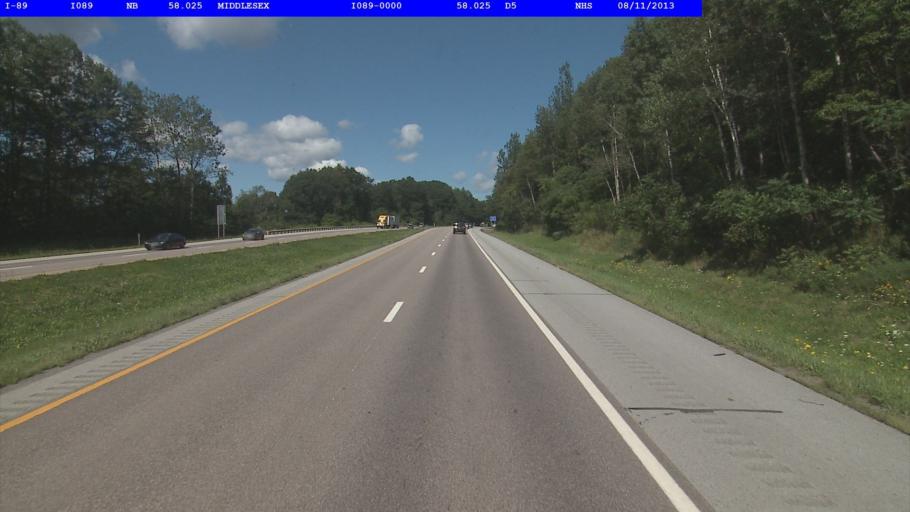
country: US
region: Vermont
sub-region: Washington County
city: Waterbury
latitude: 44.2928
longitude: -72.6736
